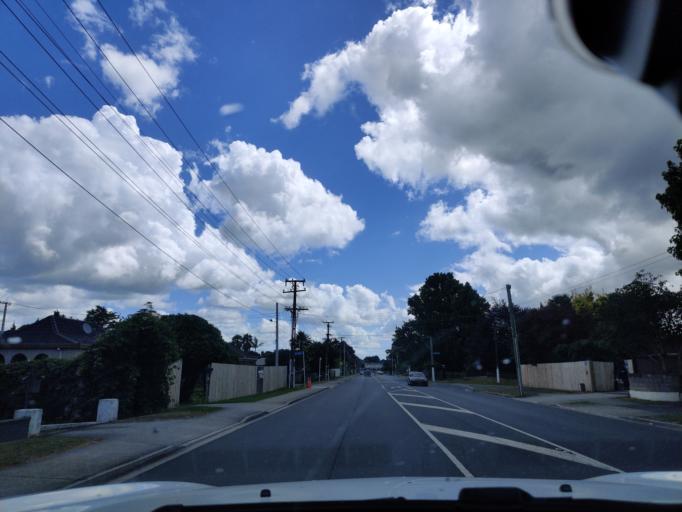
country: NZ
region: Auckland
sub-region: Auckland
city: Papakura
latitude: -37.0596
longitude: 174.9519
